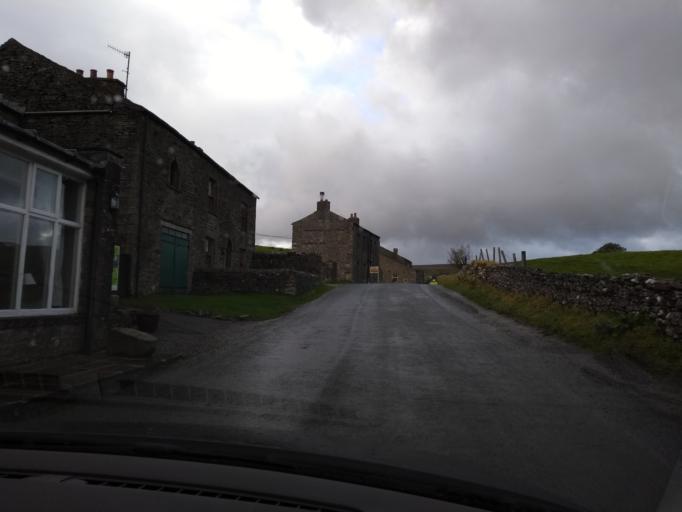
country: GB
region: England
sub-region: County Durham
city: Bowes
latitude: 54.4040
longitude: -2.1677
